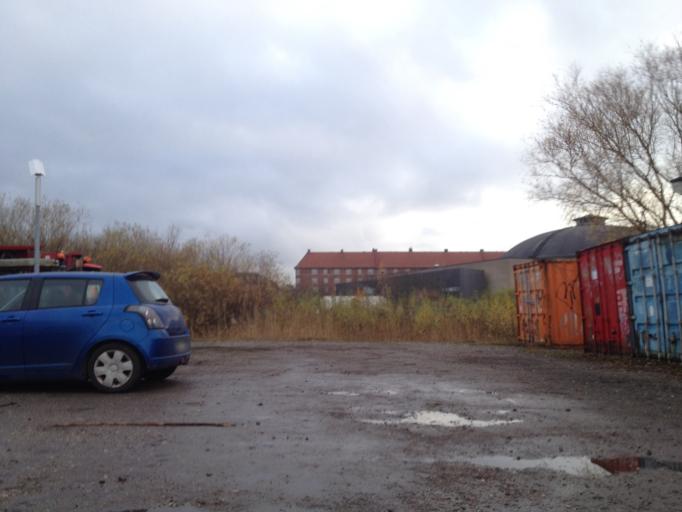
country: DK
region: Capital Region
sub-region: Kobenhavn
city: Copenhagen
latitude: 55.7116
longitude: 12.5829
